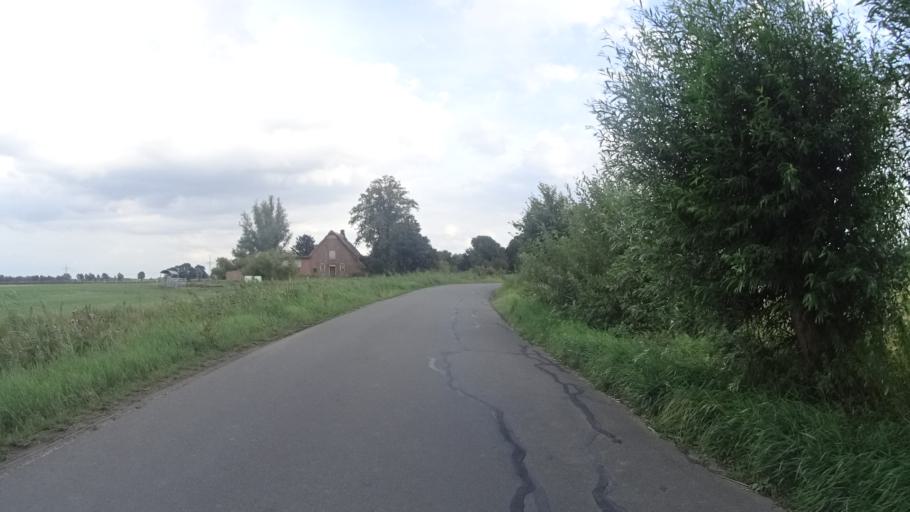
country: DE
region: Schleswig-Holstein
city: Herzhorn
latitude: 53.7753
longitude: 9.4849
